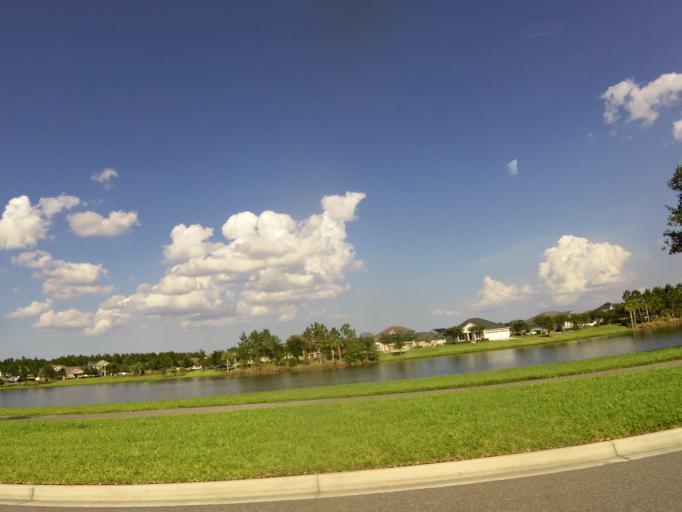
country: US
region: Florida
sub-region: Clay County
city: Green Cove Springs
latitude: 30.0258
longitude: -81.6398
